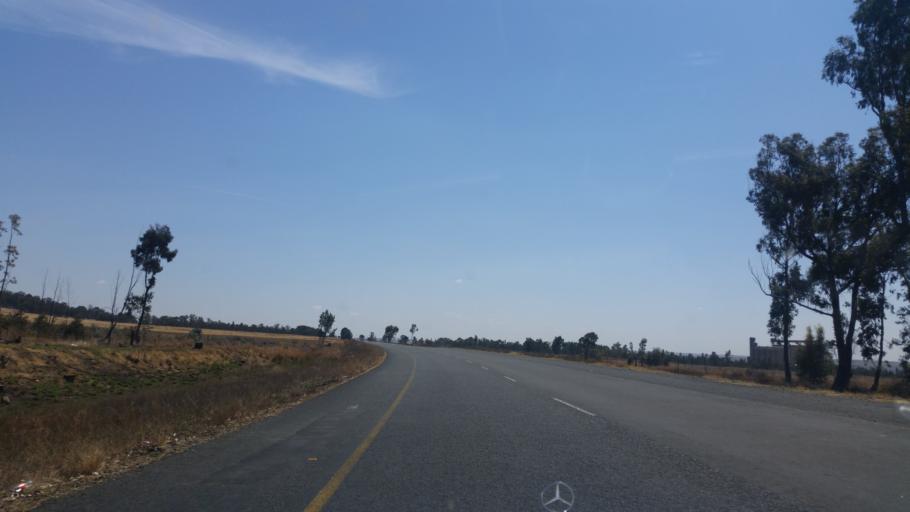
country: ZA
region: Orange Free State
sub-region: Thabo Mofutsanyana District Municipality
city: Phuthaditjhaba
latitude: -28.2215
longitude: 28.7008
